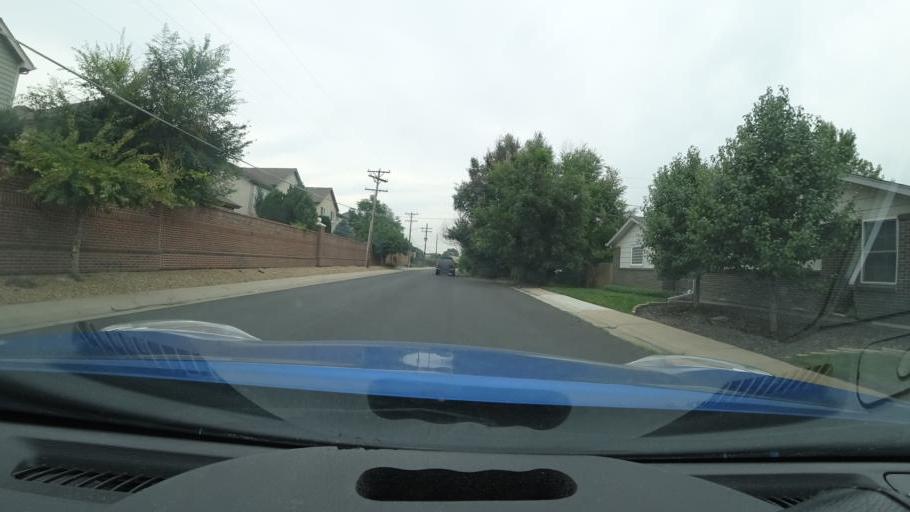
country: US
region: Colorado
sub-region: Arapahoe County
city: Glendale
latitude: 39.6839
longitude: -104.9050
